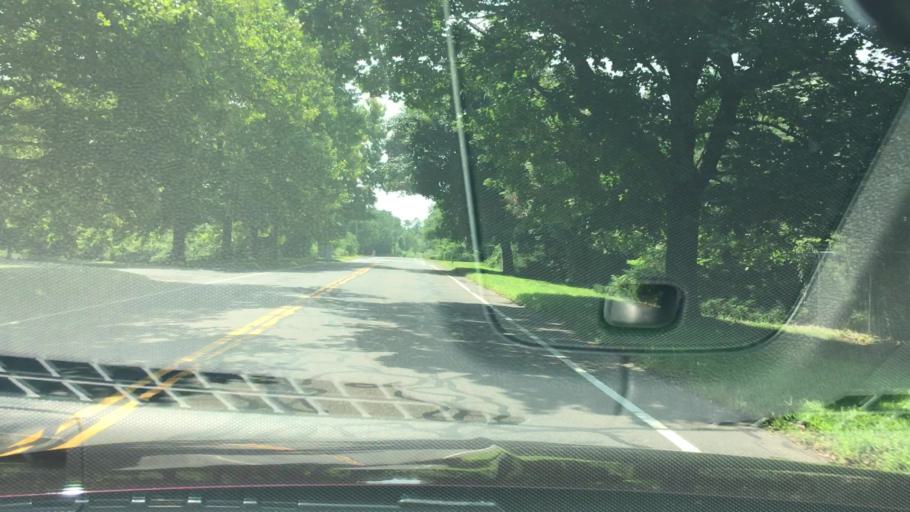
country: US
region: Connecticut
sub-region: Hartford County
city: South Windsor
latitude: 41.8292
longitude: -72.5999
